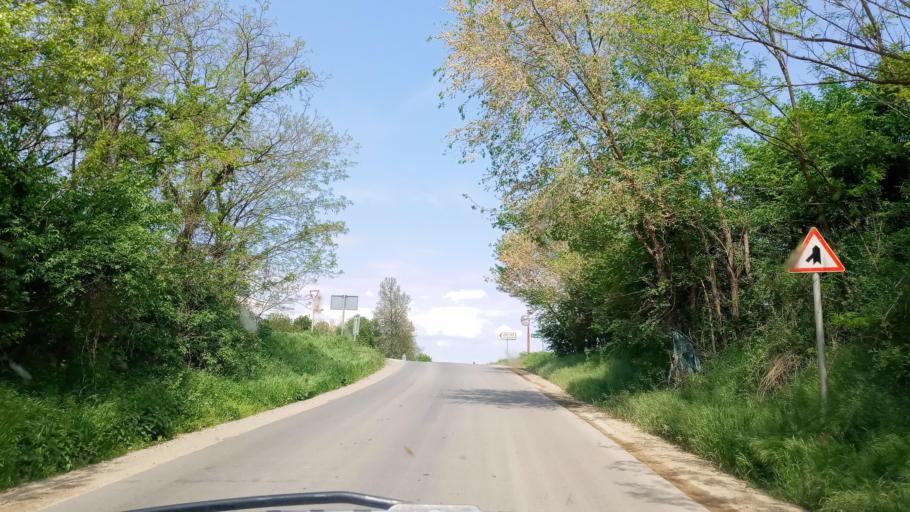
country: HU
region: Baranya
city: Boly
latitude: 45.9412
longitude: 18.5422
